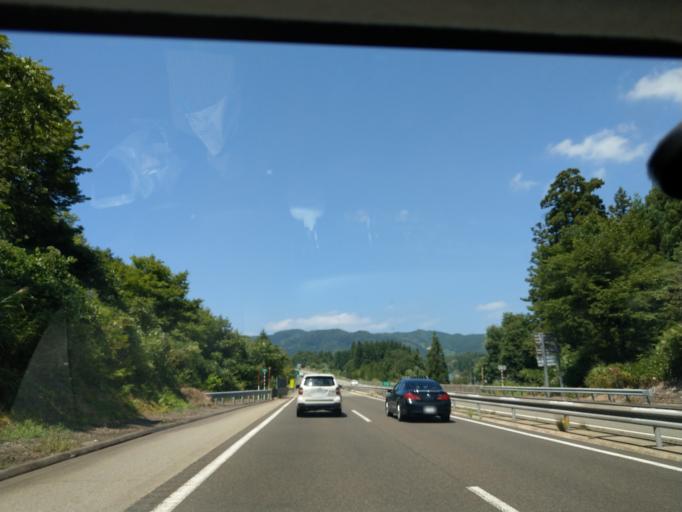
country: JP
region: Akita
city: Omagari
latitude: 39.4170
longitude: 140.4364
